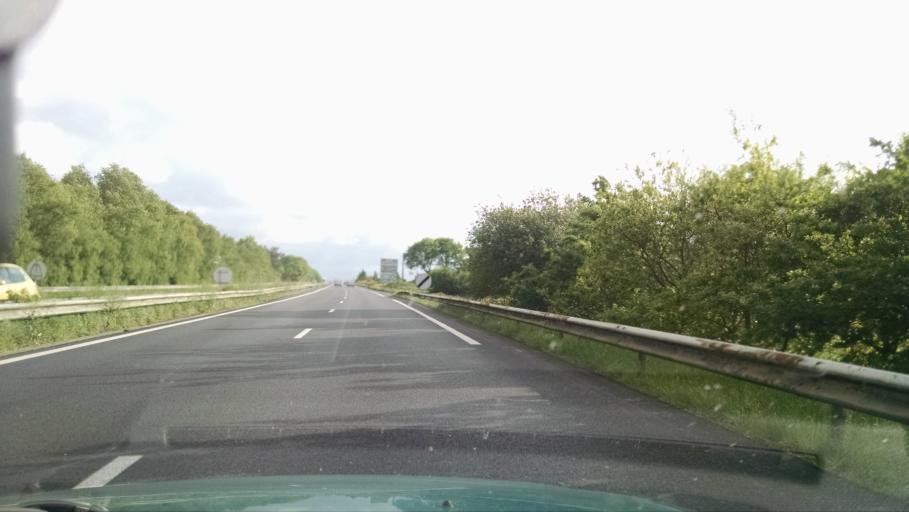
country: FR
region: Brittany
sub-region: Departement du Finistere
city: Morlaix
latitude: 48.5854
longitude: -3.8495
